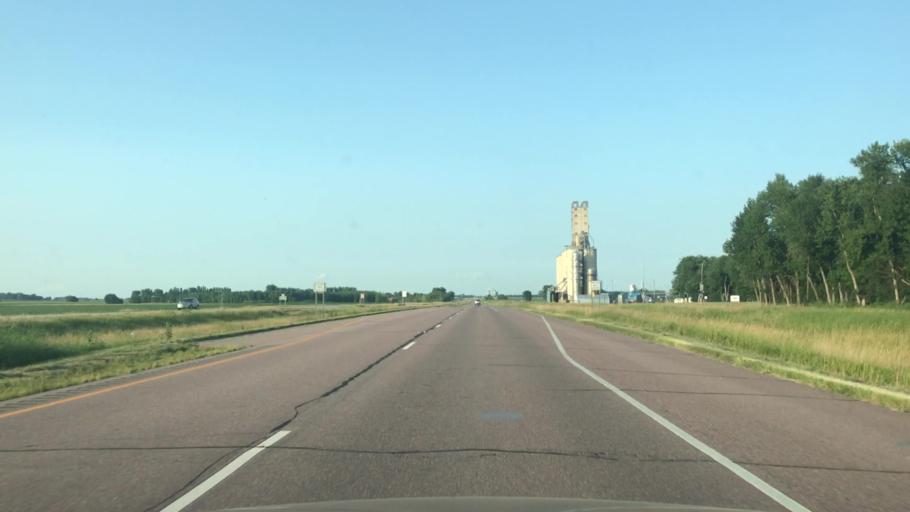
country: US
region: Minnesota
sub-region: Jackson County
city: Lakefield
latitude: 43.7651
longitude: -95.3690
